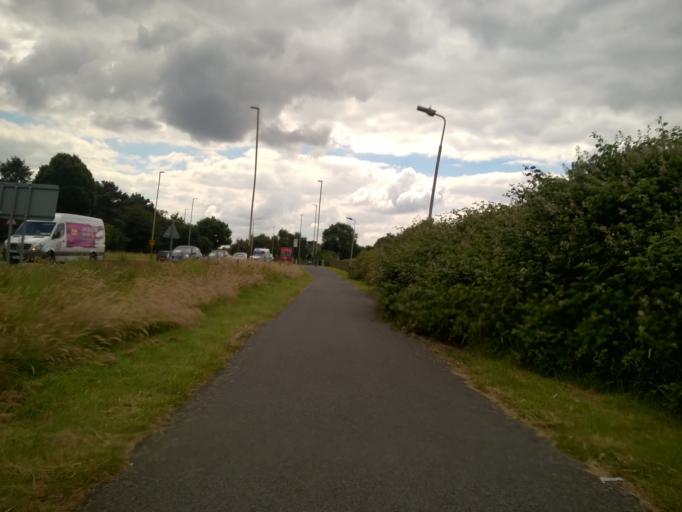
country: GB
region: England
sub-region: Leicestershire
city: Anstey
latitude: 52.6587
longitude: -1.1735
